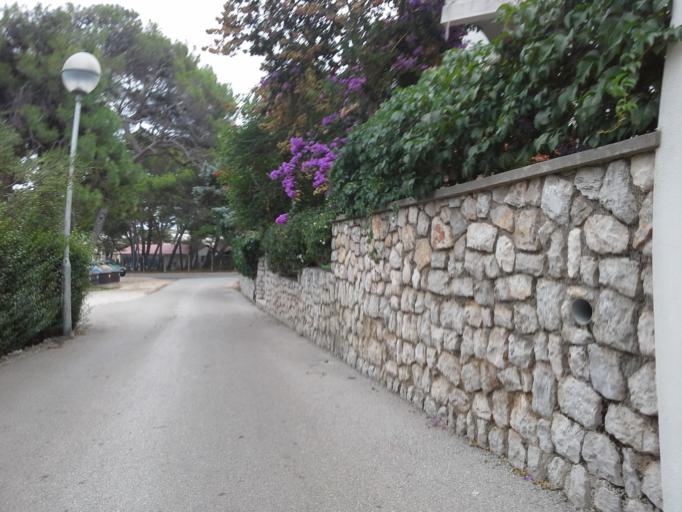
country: HR
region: Primorsko-Goranska
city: Mali Losinj
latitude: 44.5447
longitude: 14.4628
